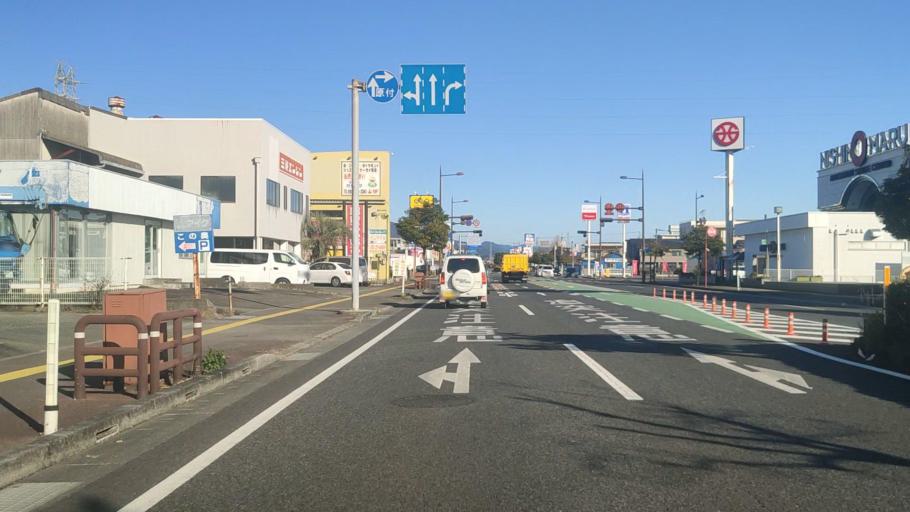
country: JP
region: Miyazaki
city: Nobeoka
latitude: 32.5711
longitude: 131.6836
